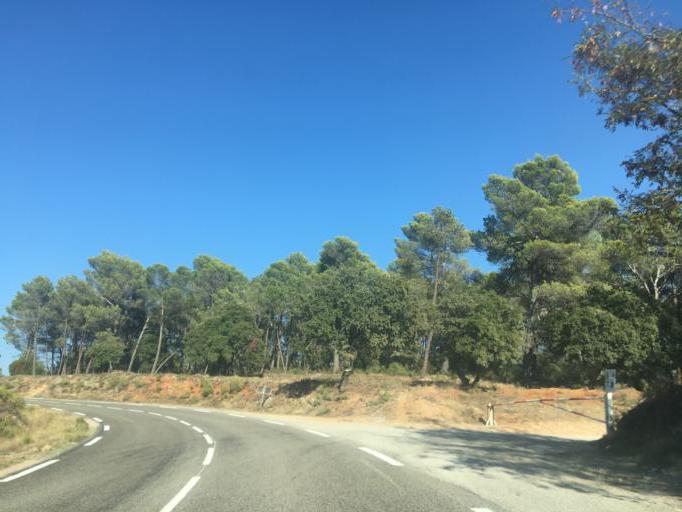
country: FR
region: Provence-Alpes-Cote d'Azur
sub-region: Departement du Var
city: Salernes
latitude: 43.5816
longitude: 6.2255
